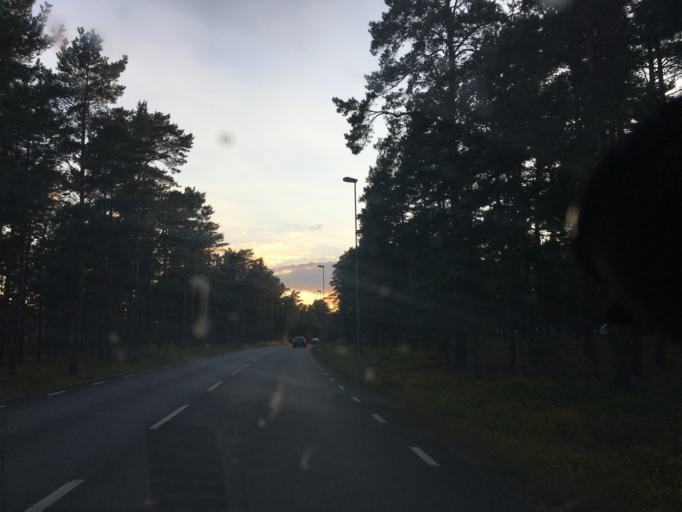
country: SE
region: Skane
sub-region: Kristianstads Kommun
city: Ahus
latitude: 55.9412
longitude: 14.3112
